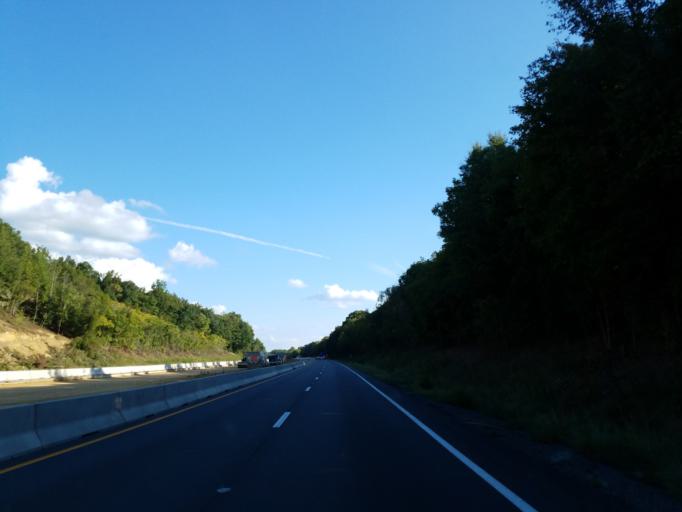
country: US
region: North Carolina
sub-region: Rowan County
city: Landis
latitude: 35.5191
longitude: -80.5705
